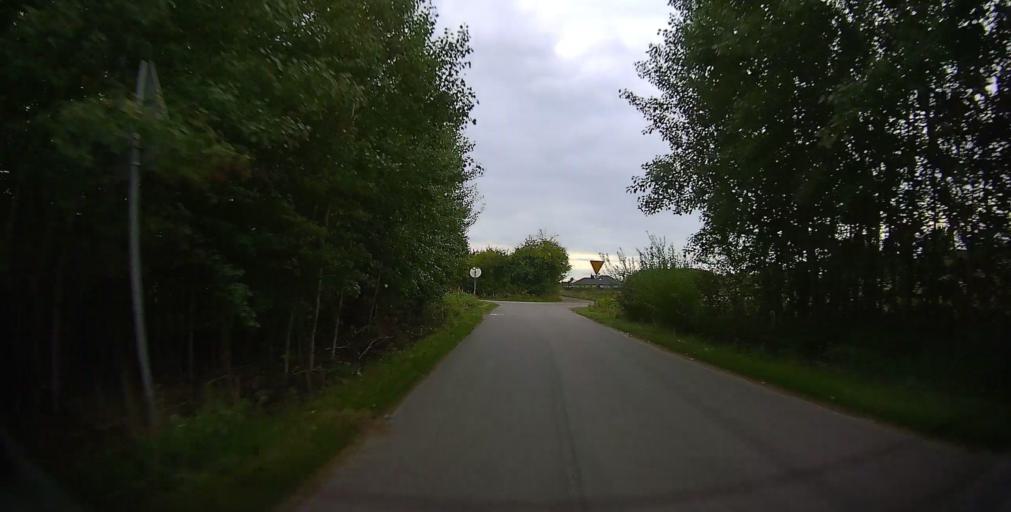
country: PL
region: Masovian Voivodeship
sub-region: Powiat radomski
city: Jedlinsk
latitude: 51.4536
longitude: 21.1044
